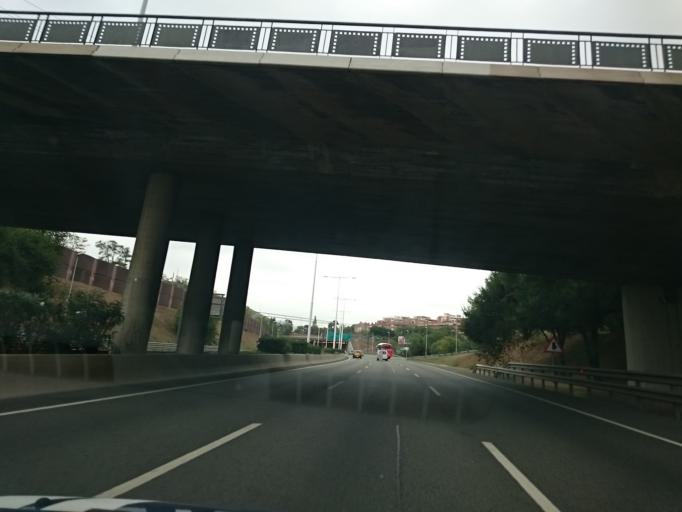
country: ES
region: Catalonia
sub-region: Provincia de Barcelona
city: Esplugues de Llobregat
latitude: 41.3702
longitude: 2.0925
